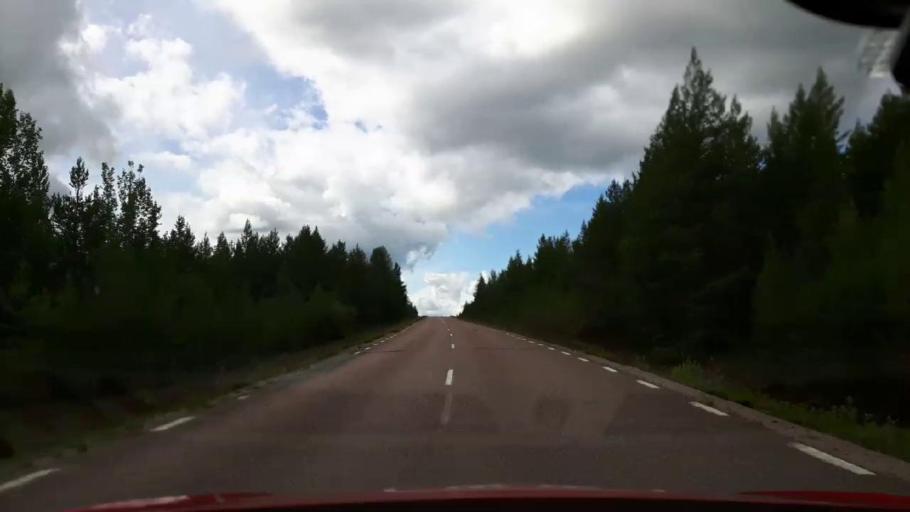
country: SE
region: Jaemtland
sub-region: Harjedalens Kommun
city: Sveg
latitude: 61.8291
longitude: 13.8795
